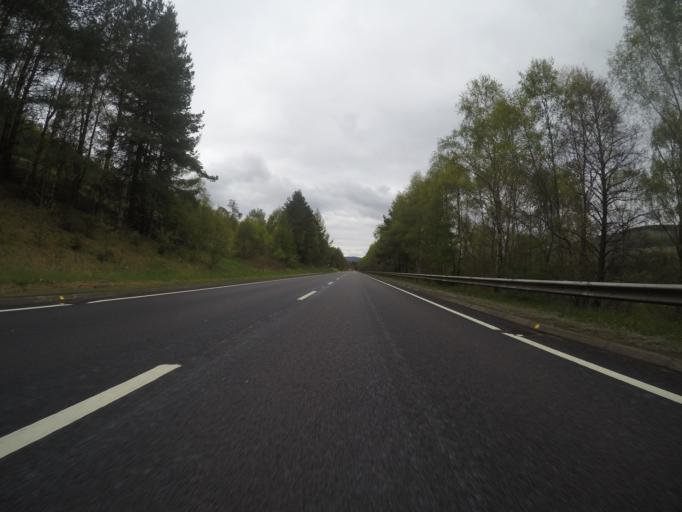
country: GB
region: Scotland
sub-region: Perth and Kinross
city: Aberfeldy
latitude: 56.7648
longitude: -3.8719
